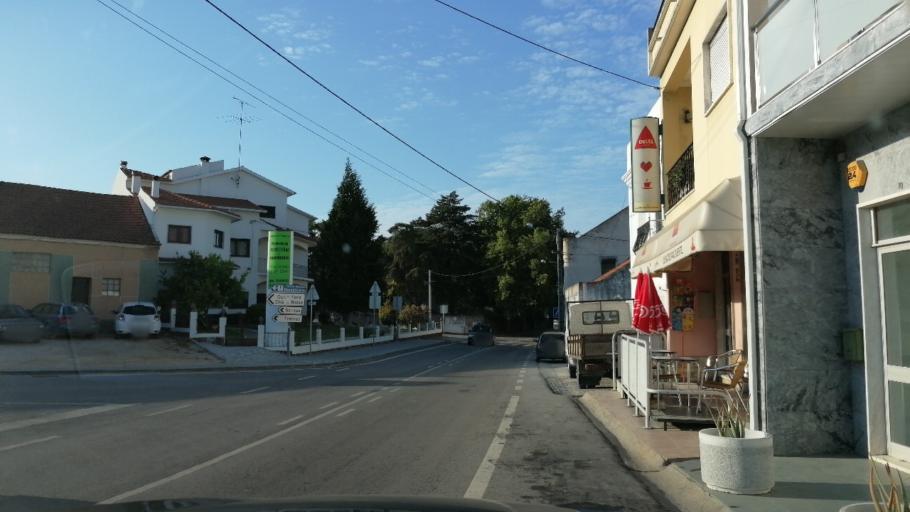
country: PT
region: Santarem
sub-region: Alcanena
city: Alcanena
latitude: 39.3796
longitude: -8.6608
